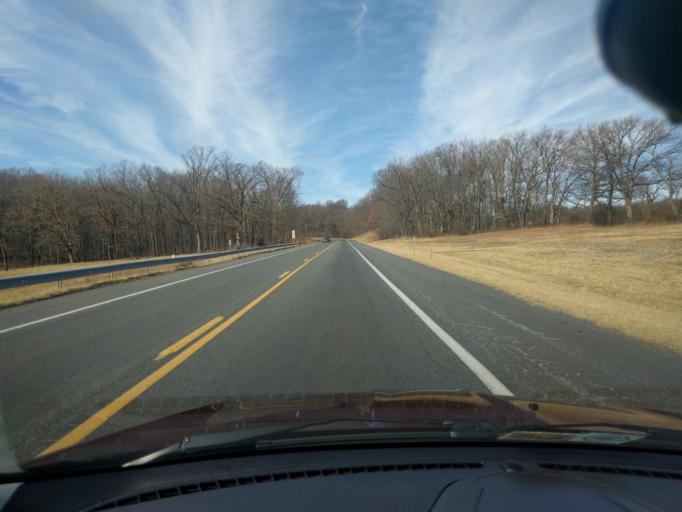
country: US
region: Virginia
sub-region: Augusta County
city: Verona
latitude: 38.1854
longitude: -79.0378
